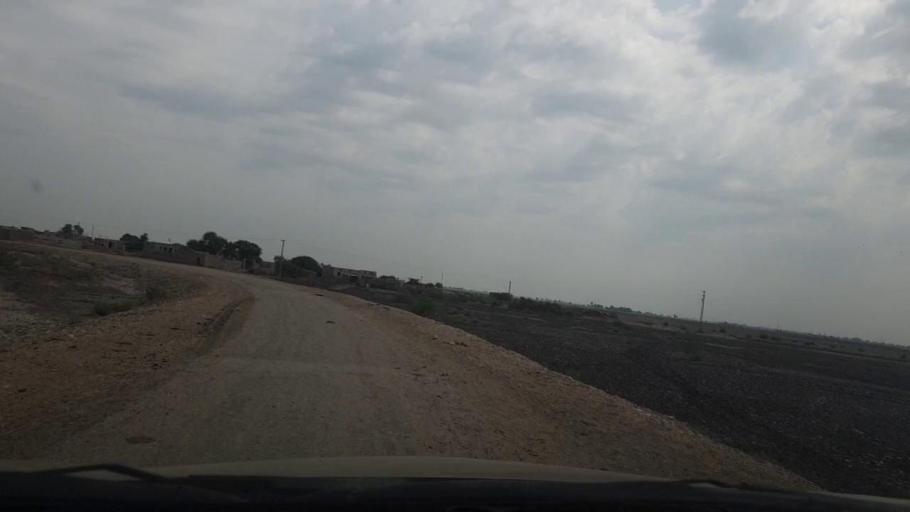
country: PK
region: Sindh
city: Ratodero
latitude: 27.6989
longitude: 68.2293
